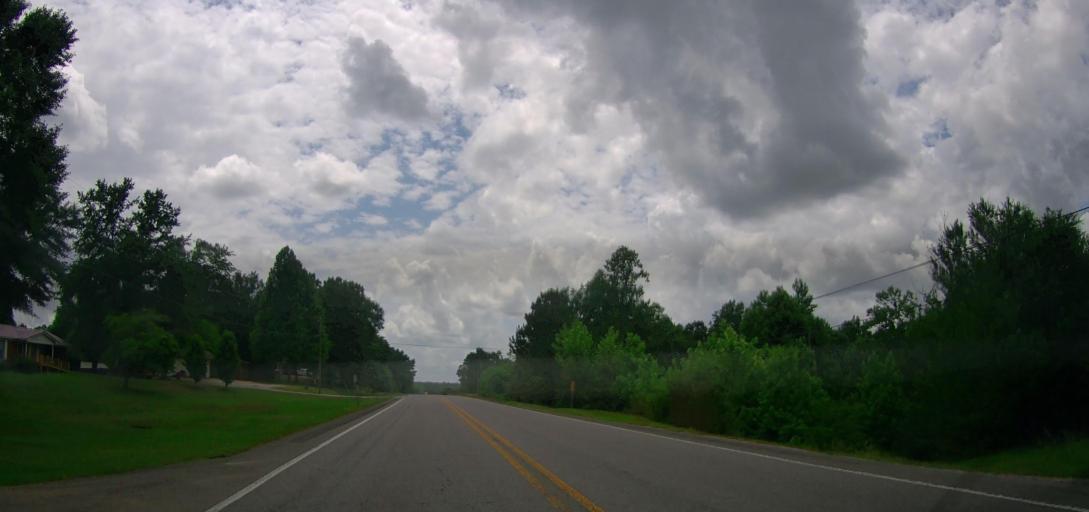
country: US
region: Alabama
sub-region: Marion County
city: Hamilton
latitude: 34.1356
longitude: -88.0191
